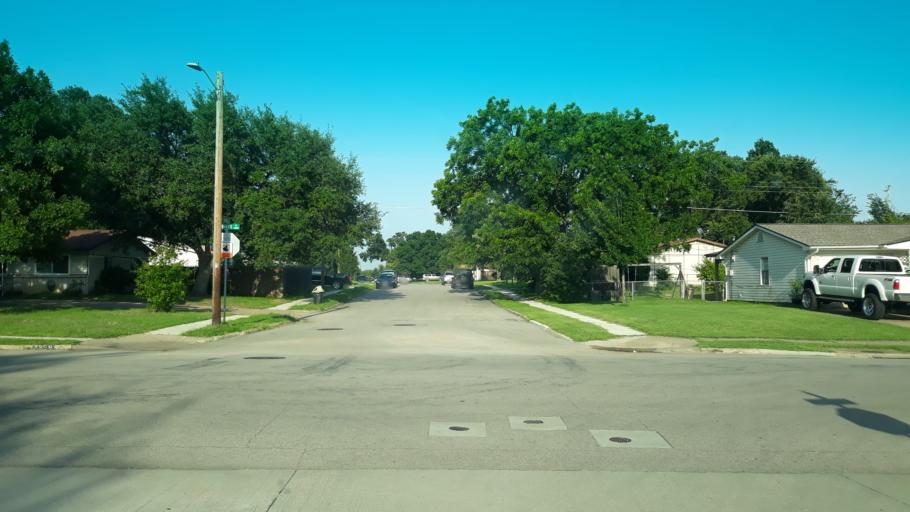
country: US
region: Texas
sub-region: Dallas County
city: Irving
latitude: 32.8541
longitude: -96.9857
